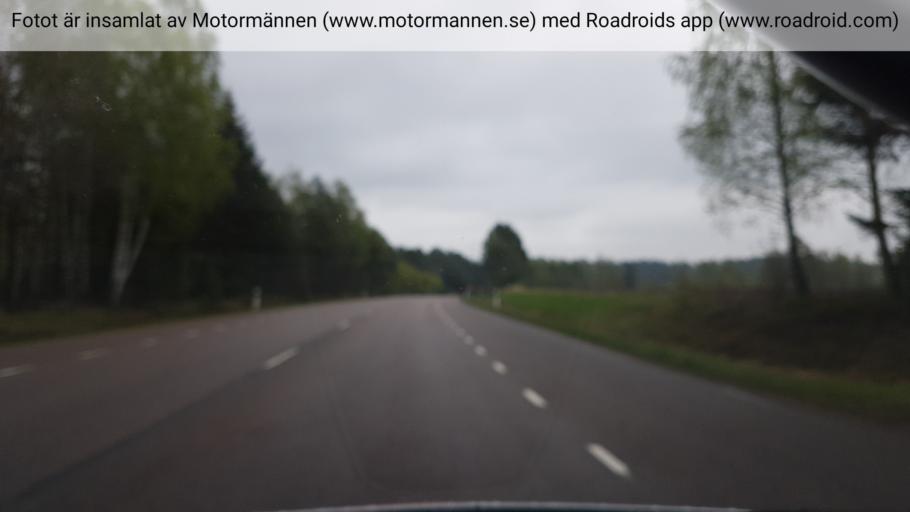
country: SE
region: Vaestra Goetaland
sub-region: Skovde Kommun
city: Stopen
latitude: 58.4324
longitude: 13.9195
